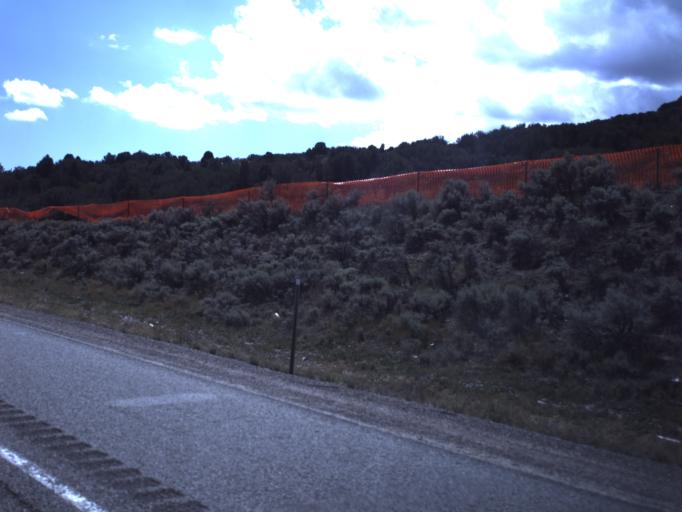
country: US
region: Utah
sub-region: Wayne County
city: Loa
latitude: 38.7800
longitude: -111.4851
